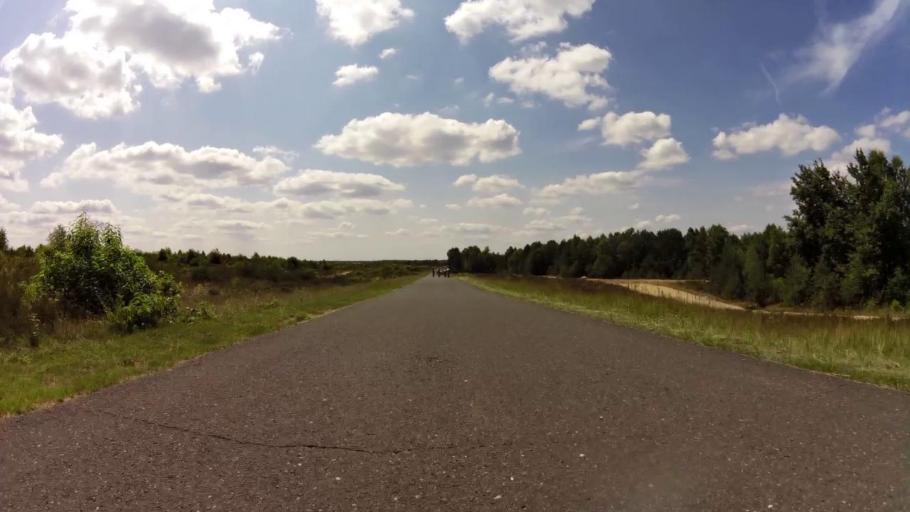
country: PL
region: West Pomeranian Voivodeship
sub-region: Powiat drawski
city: Drawsko Pomorskie
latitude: 53.4325
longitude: 15.7514
